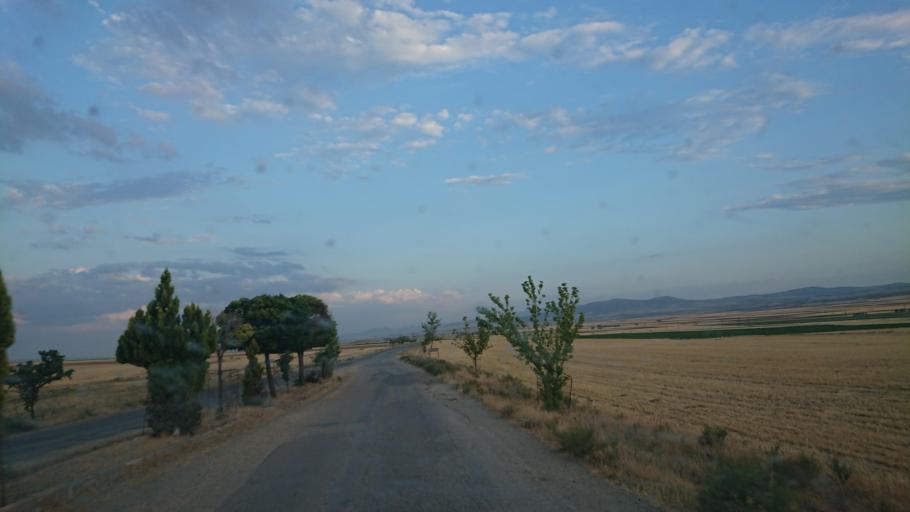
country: TR
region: Aksaray
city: Agacoren
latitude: 38.9199
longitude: 34.0356
